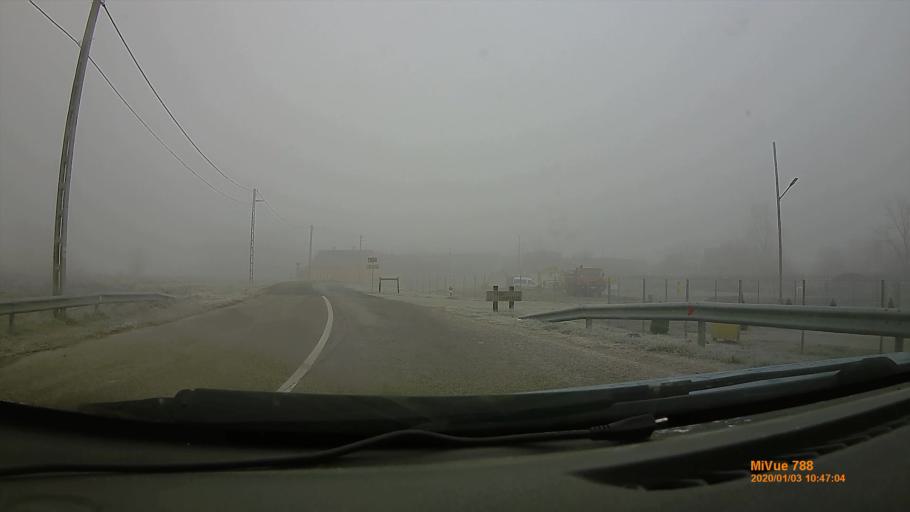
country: HU
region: Tolna
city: Bataszek
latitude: 46.2064
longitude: 18.7320
